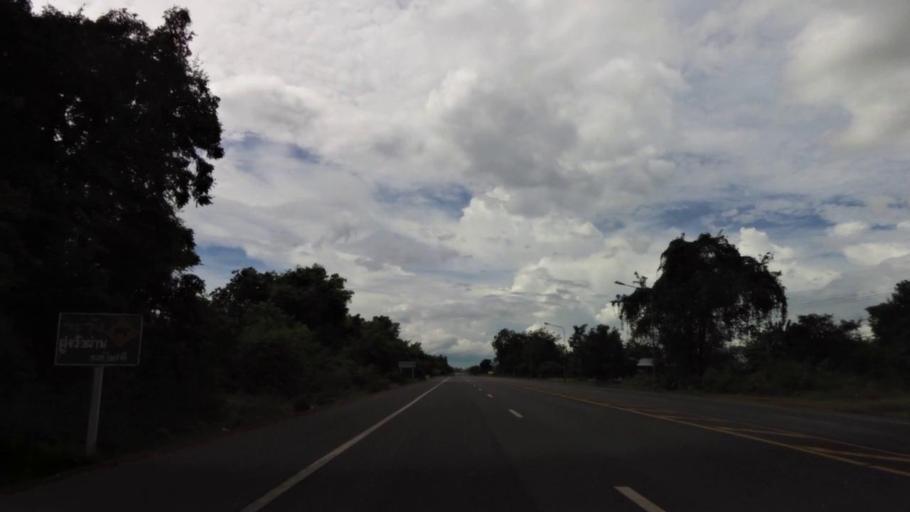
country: TH
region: Nakhon Sawan
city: Phai Sali
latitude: 15.5993
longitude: 100.6690
